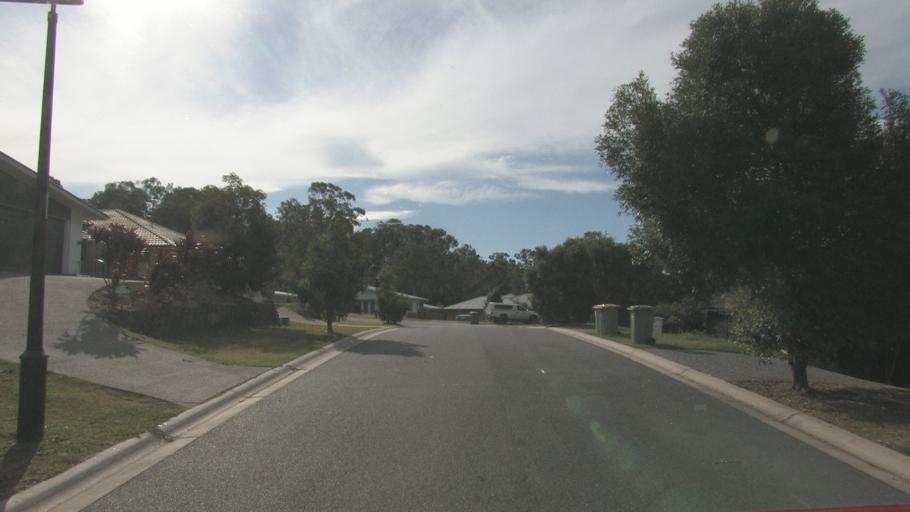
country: AU
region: Queensland
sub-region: Logan
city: Windaroo
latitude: -27.7478
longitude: 153.1856
